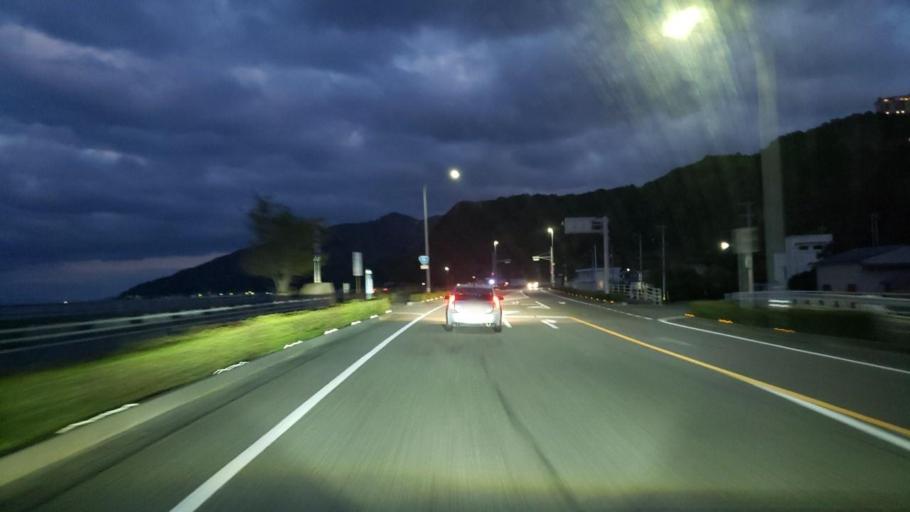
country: JP
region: Tokushima
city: Ishii
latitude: 34.2071
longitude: 134.4616
